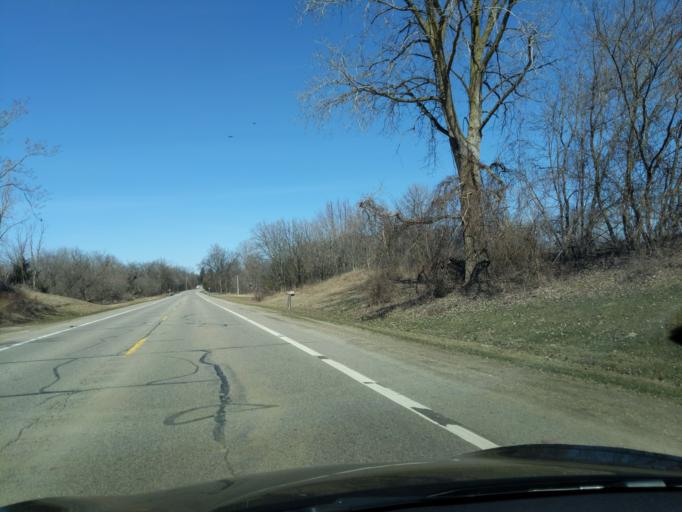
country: US
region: Michigan
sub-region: Ionia County
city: Lake Odessa
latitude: 42.7203
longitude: -85.0949
